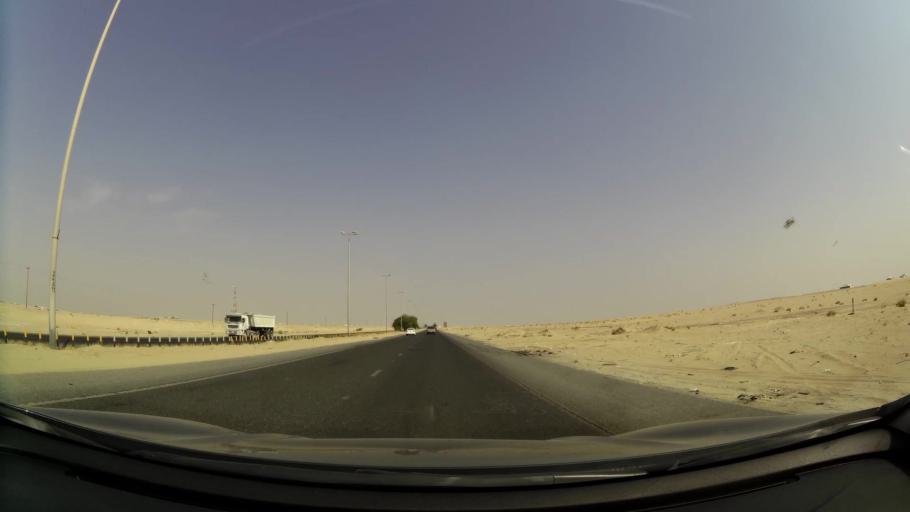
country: KW
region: Al Ahmadi
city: Al Wafrah
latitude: 28.8357
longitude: 48.0564
